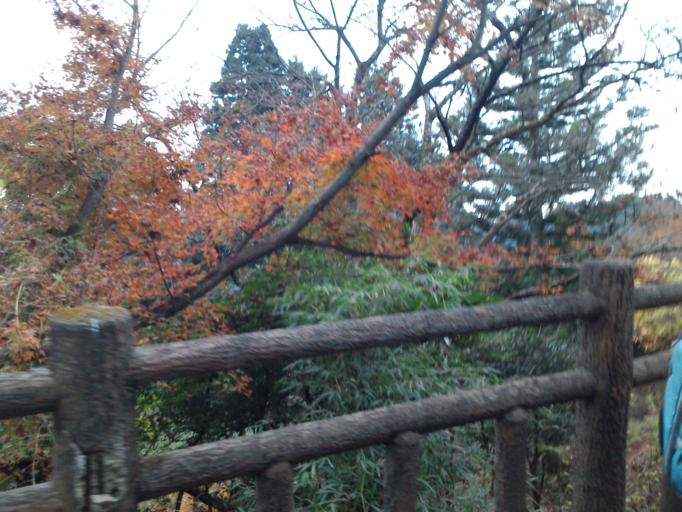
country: JP
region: Tokyo
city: Ome
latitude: 35.7893
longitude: 139.1533
